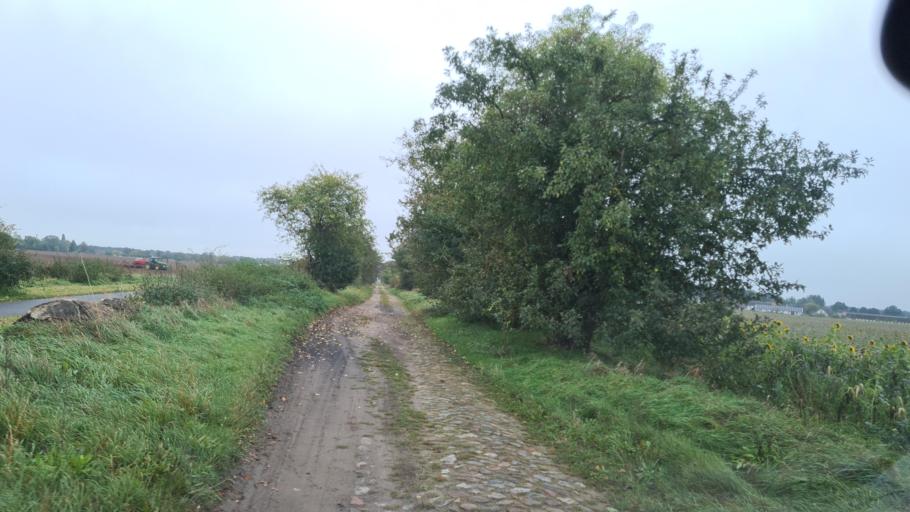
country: DE
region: Brandenburg
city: Furstenwalde
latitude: 52.4105
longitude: 14.0349
